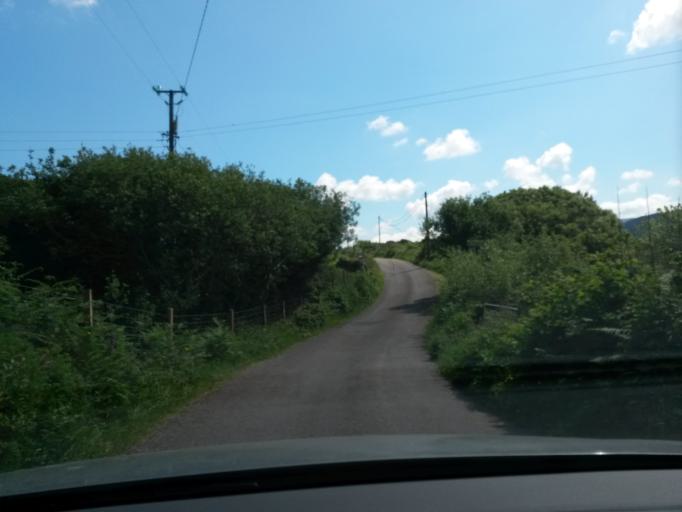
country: IE
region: Munster
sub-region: Ciarrai
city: Cahersiveen
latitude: 51.7178
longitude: -9.9577
